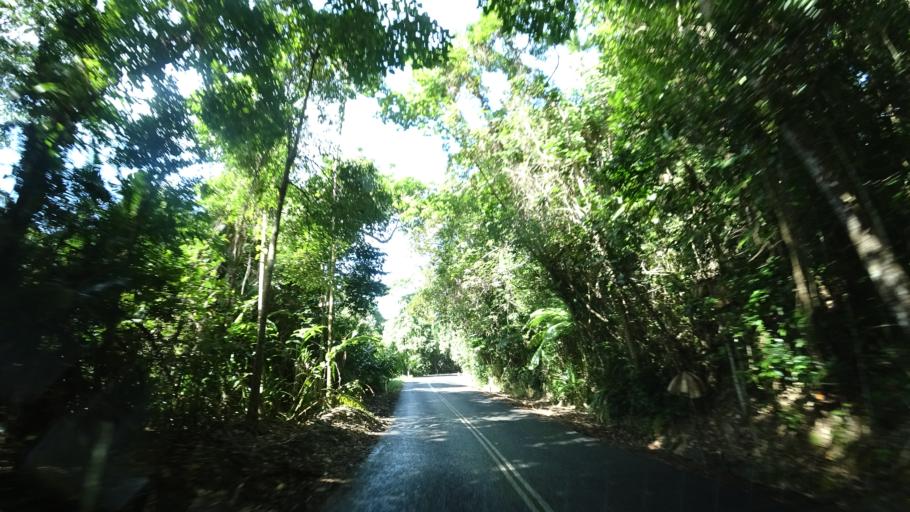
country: AU
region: Queensland
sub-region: Cairns
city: Port Douglas
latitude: -16.1114
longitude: 145.4567
